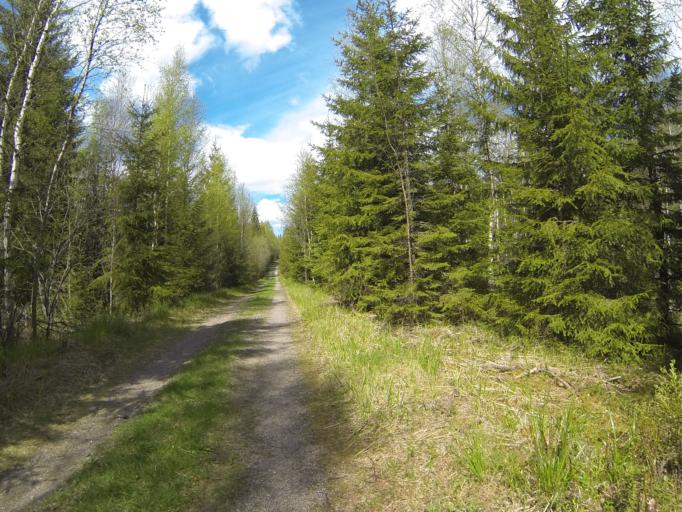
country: FI
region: Varsinais-Suomi
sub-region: Salo
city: Halikko
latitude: 60.3028
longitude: 23.0760
